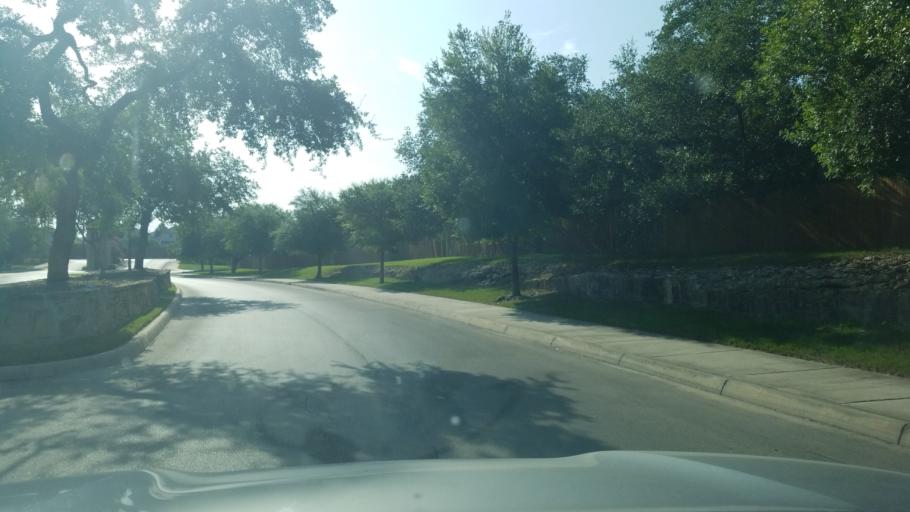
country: US
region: Texas
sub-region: Medina County
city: La Coste
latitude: 29.4344
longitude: -98.7497
